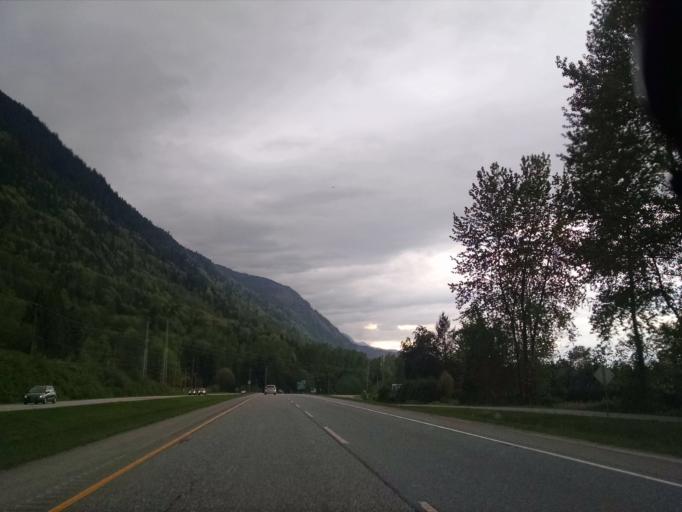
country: CA
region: British Columbia
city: Agassiz
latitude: 49.2109
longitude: -121.7066
